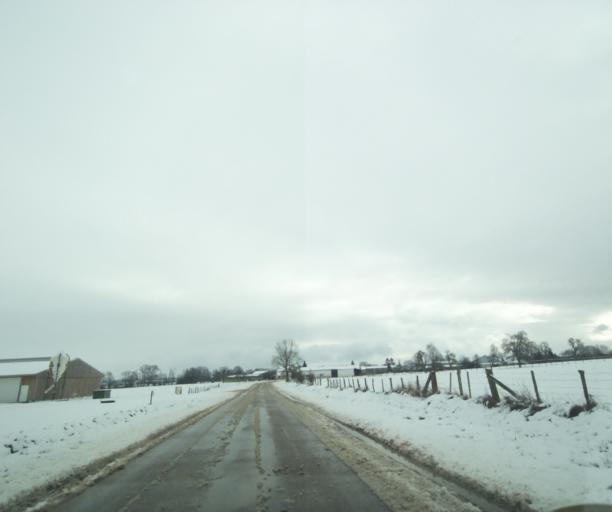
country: FR
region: Champagne-Ardenne
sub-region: Departement de la Haute-Marne
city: Montier-en-Der
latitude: 48.4403
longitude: 4.7094
